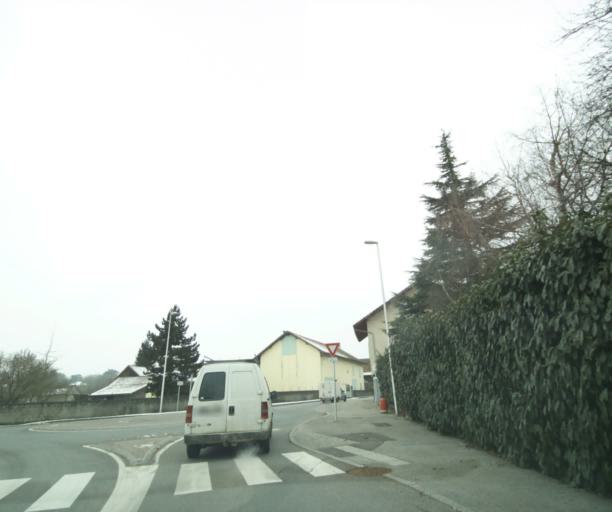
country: FR
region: Rhone-Alpes
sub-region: Departement de la Haute-Savoie
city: Reignier-Esery
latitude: 46.1335
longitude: 6.2657
